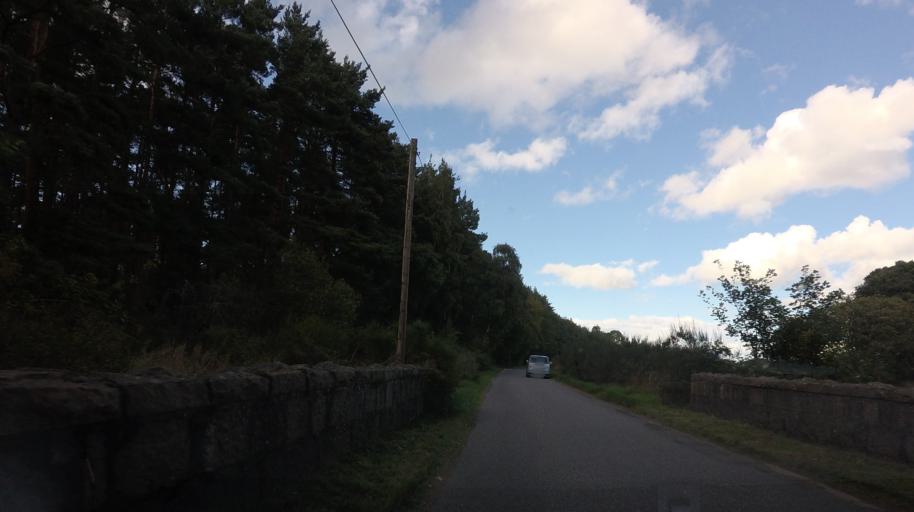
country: GB
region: Scotland
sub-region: Aberdeenshire
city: Banchory
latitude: 57.0838
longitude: -2.4542
